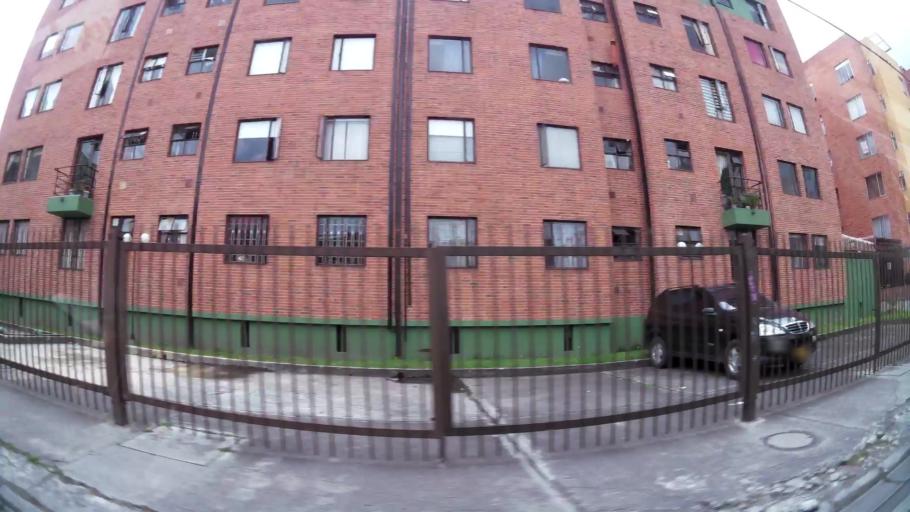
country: CO
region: Cundinamarca
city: Cota
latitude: 4.7472
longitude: -74.0501
